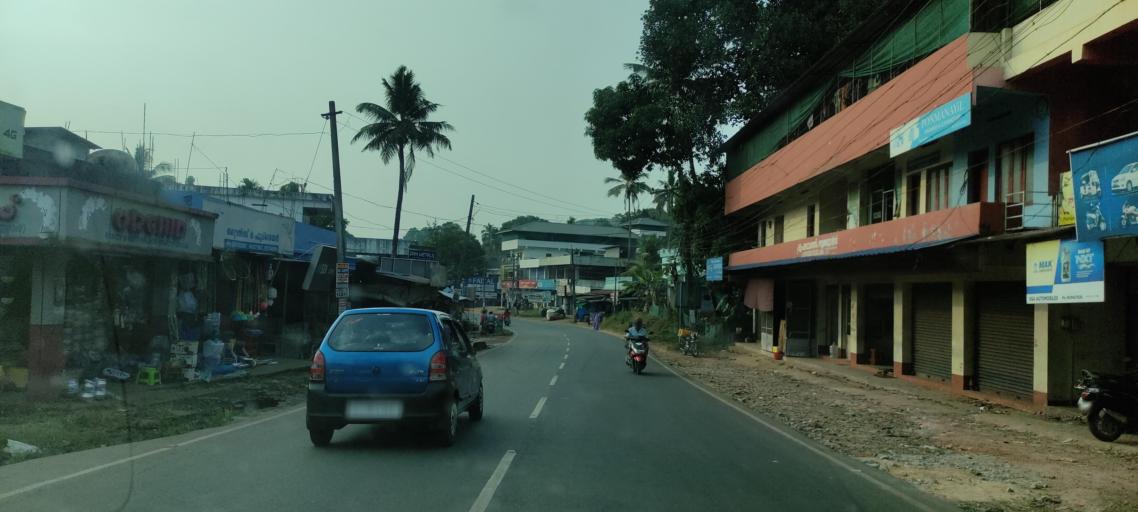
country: IN
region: Kerala
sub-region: Pattanamtitta
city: Adur
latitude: 9.1655
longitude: 76.6839
